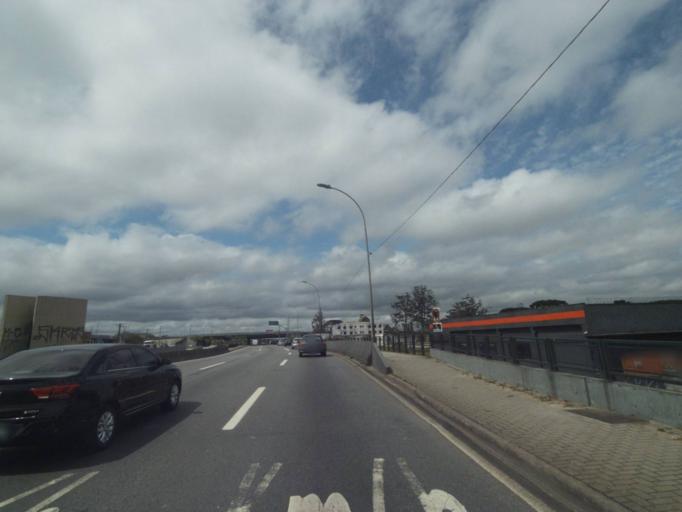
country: BR
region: Parana
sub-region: Curitiba
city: Curitiba
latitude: -25.4412
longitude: -49.2338
